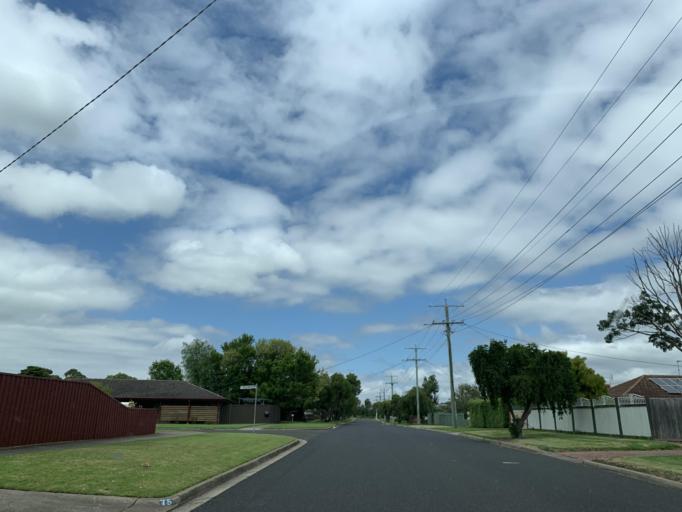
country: AU
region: Victoria
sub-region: Wellington
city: Sale
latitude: -38.1092
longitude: 147.0918
